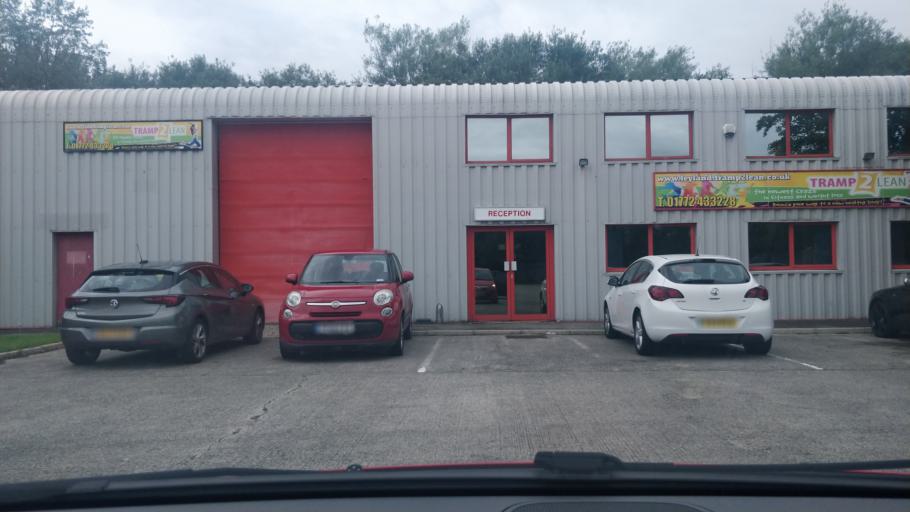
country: GB
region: England
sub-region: Lancashire
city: Leyland
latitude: 53.6978
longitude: -2.7287
